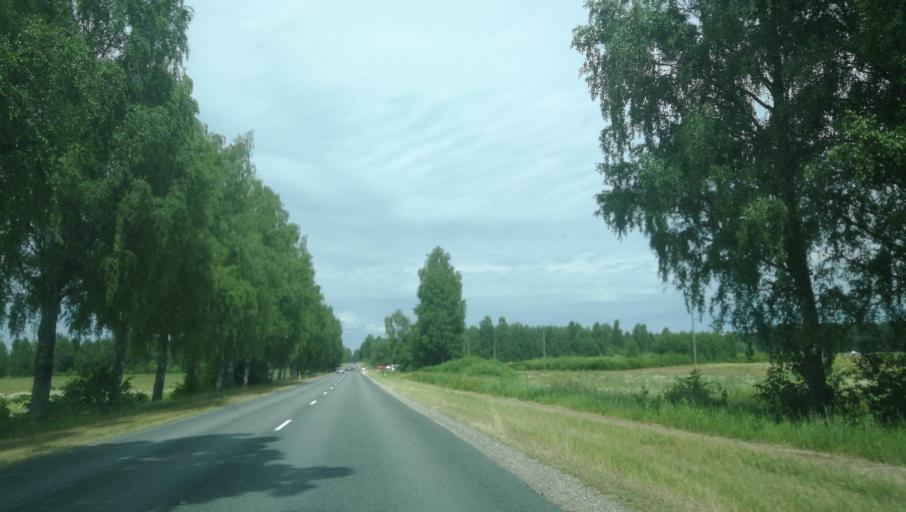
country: LV
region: Valmieras Rajons
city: Valmiera
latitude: 57.6159
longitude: 25.4533
